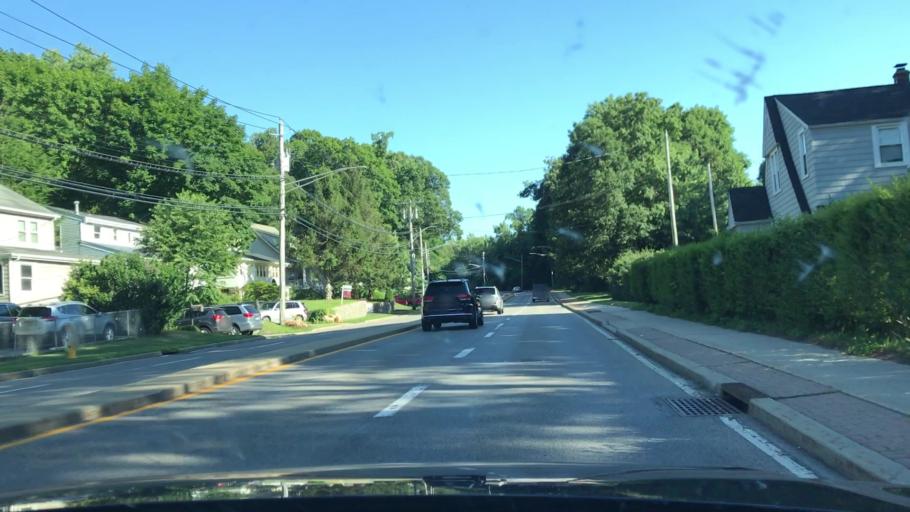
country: US
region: New York
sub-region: Westchester County
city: Thornwood
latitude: 41.1216
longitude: -73.7757
